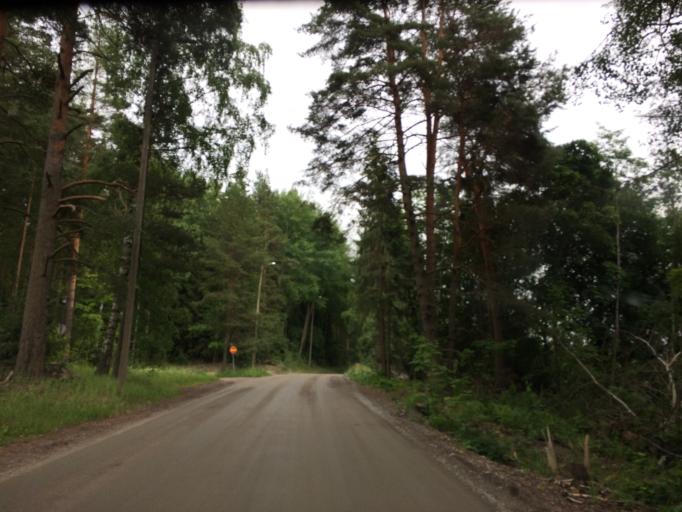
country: FI
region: Haeme
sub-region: Haemeenlinna
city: Haemeenlinna
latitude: 60.9677
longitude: 24.5248
